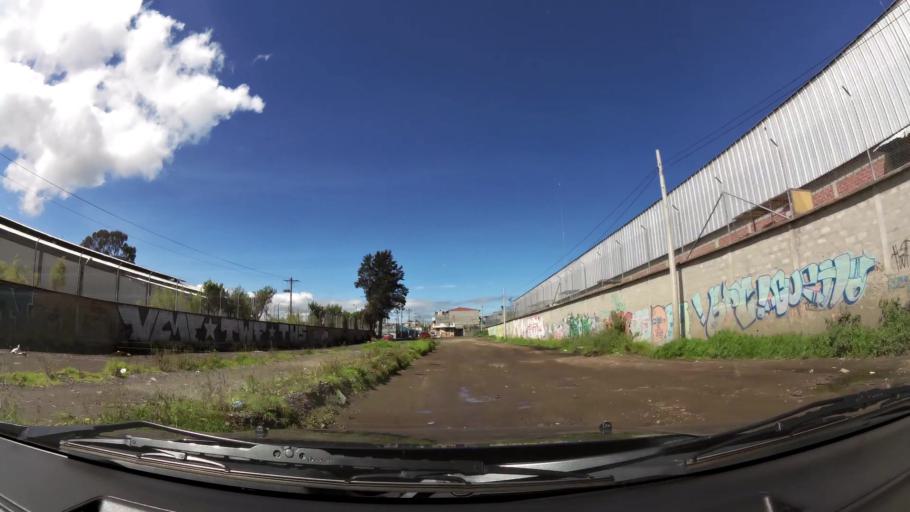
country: EC
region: Pichincha
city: Quito
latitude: -0.3024
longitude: -78.5478
